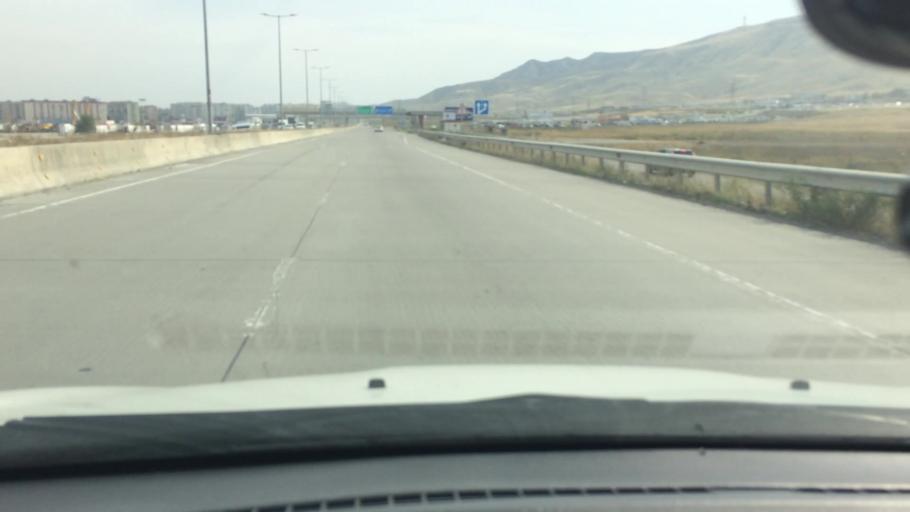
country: GE
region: Kvemo Kartli
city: Rust'avi
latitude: 41.5787
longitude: 44.9547
